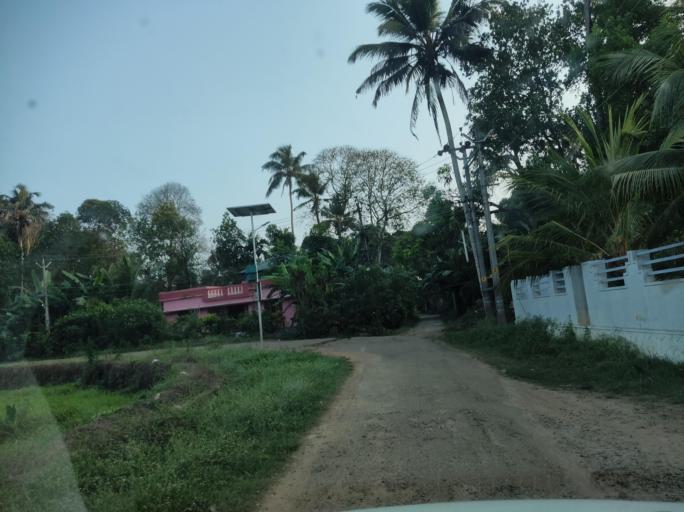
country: IN
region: Kerala
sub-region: Pattanamtitta
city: Tiruvalla
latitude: 9.3615
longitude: 76.5648
